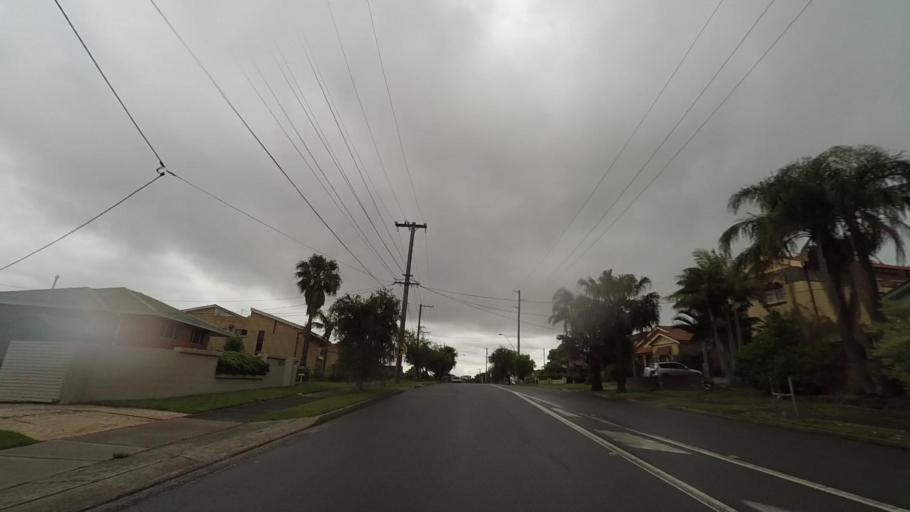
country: AU
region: New South Wales
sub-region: Rockdale
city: Ramsgate
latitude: -33.9880
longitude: 151.1311
